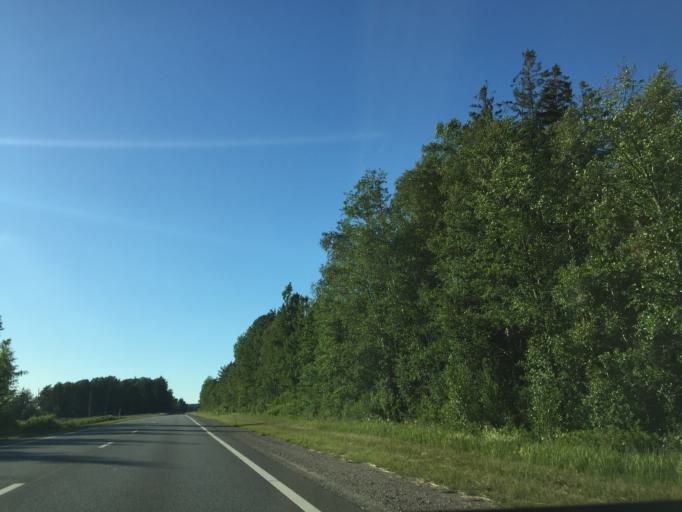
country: LV
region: Ventspils
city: Ventspils
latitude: 57.3842
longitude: 21.7088
